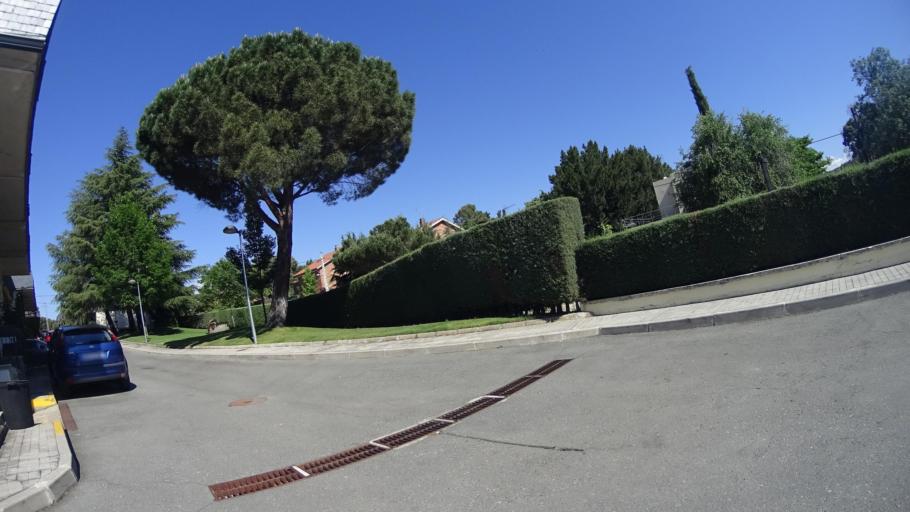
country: ES
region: Madrid
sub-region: Provincia de Madrid
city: Galapagar
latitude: 40.5835
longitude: -3.9668
